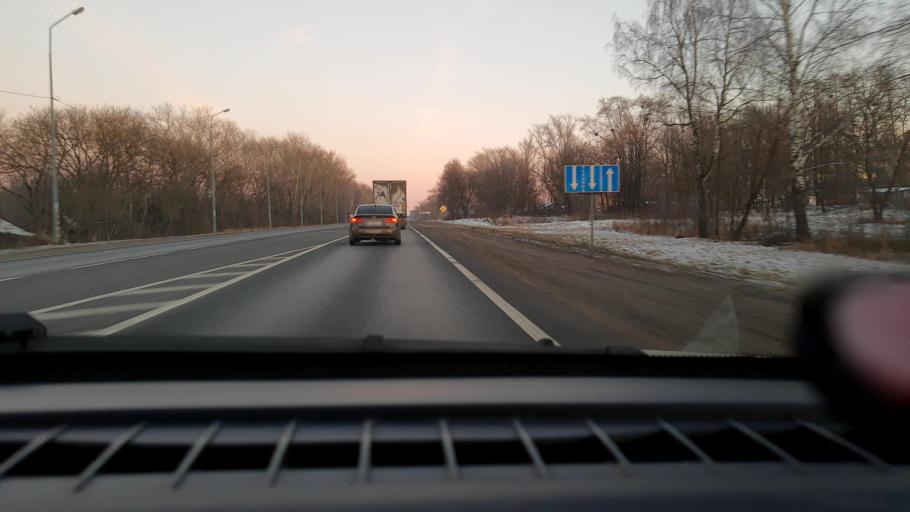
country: RU
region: Nizjnij Novgorod
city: Pamyat' Parizhskoy Kommuny
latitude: 56.0421
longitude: 44.4468
